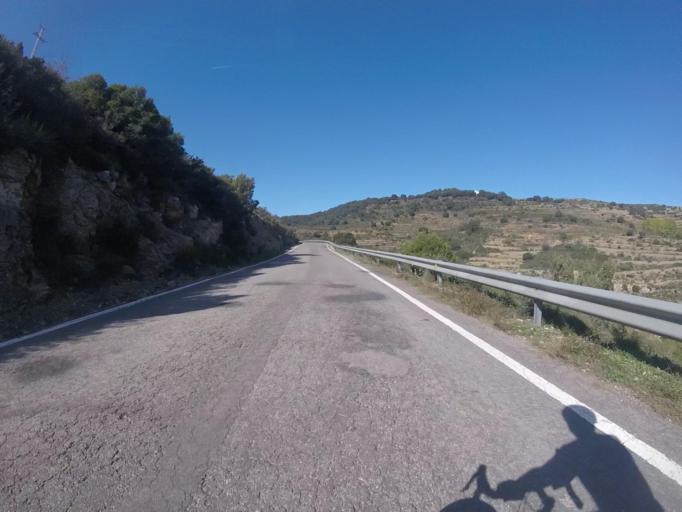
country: ES
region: Valencia
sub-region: Provincia de Castello
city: Sarratella
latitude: 40.3169
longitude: 0.0294
